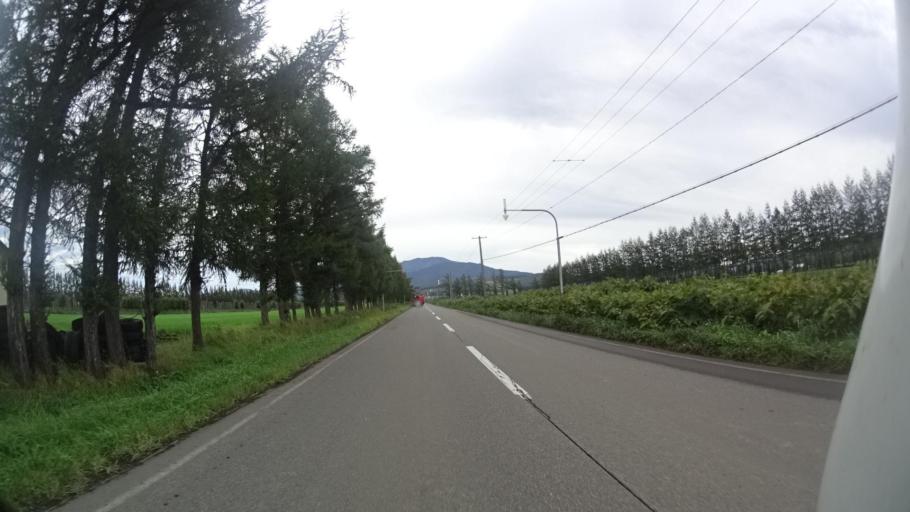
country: JP
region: Hokkaido
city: Shibetsu
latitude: 43.8738
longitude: 144.7331
